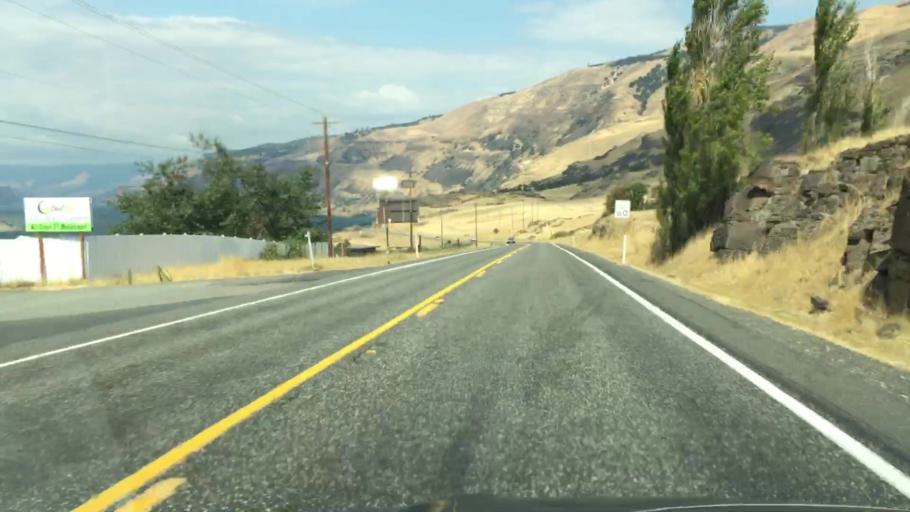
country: US
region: Washington
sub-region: Klickitat County
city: Dallesport
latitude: 45.6582
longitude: -121.1934
